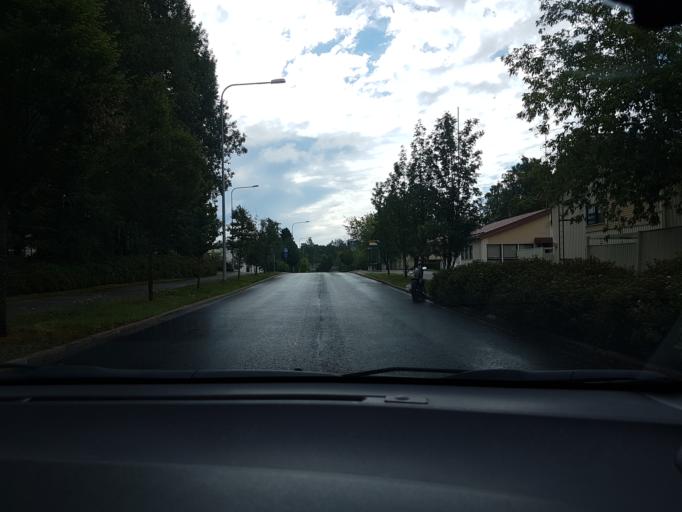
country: FI
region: Uusimaa
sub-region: Helsinki
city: Vantaa
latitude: 60.2200
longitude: 25.1137
